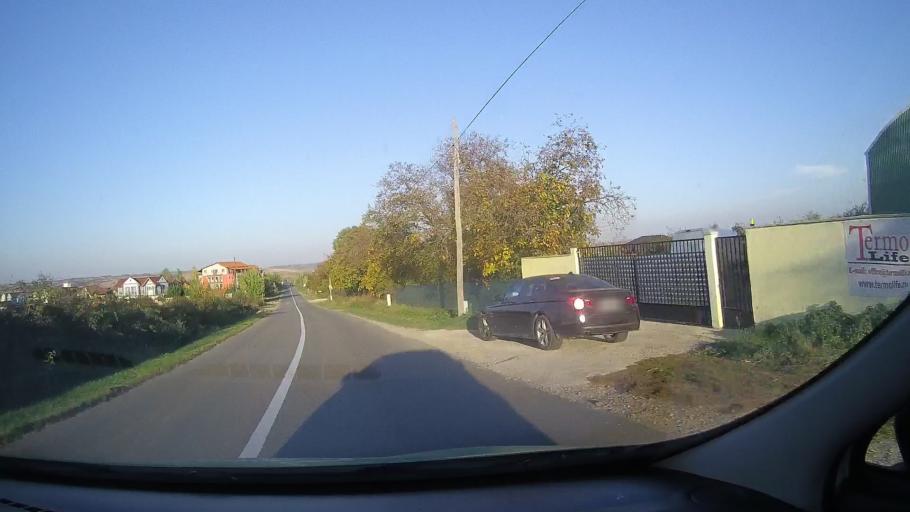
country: RO
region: Bihor
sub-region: Comuna Paleu
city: Paleu
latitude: 47.1098
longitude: 21.9336
